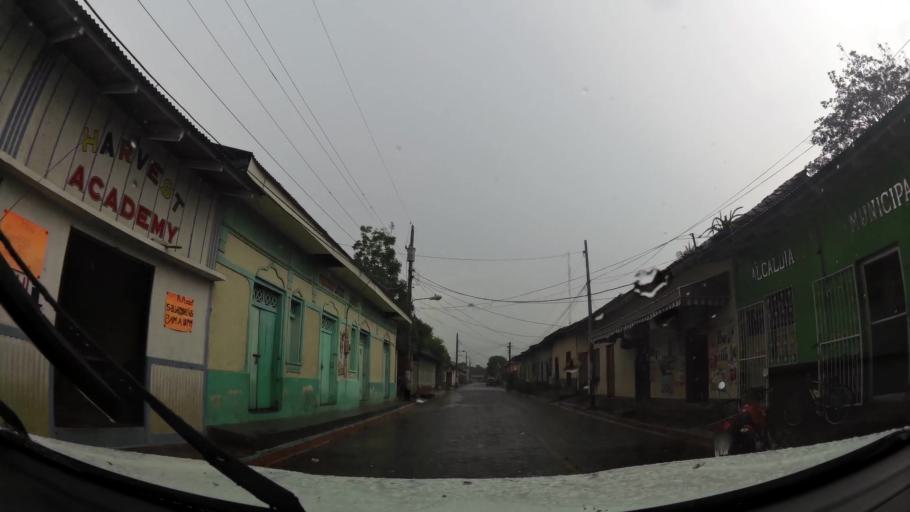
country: NI
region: Leon
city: Telica
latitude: 12.5217
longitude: -86.8583
